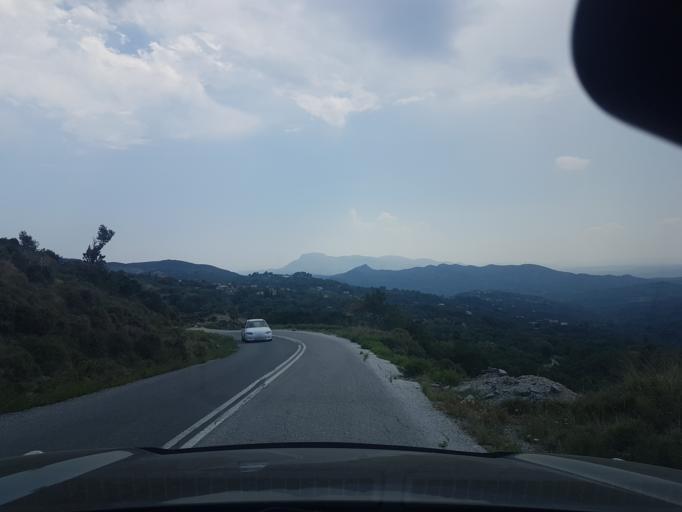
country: GR
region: Central Greece
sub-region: Nomos Evvoias
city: Kymi
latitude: 38.6433
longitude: 24.0621
